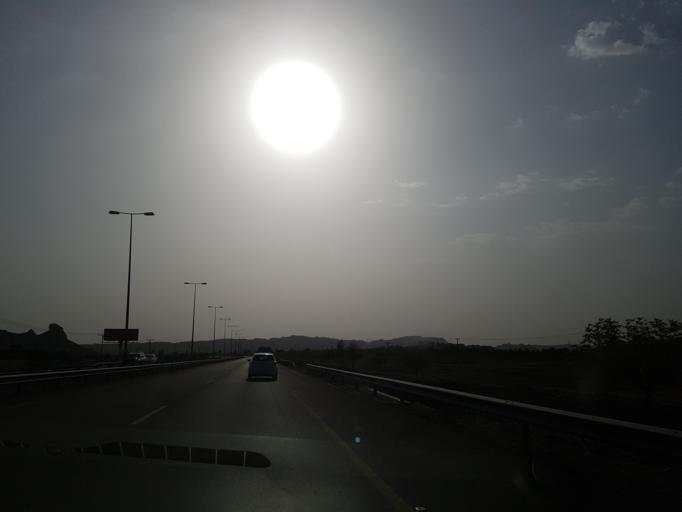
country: OM
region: Al Buraimi
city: Al Buraymi
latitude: 24.2440
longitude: 55.9860
